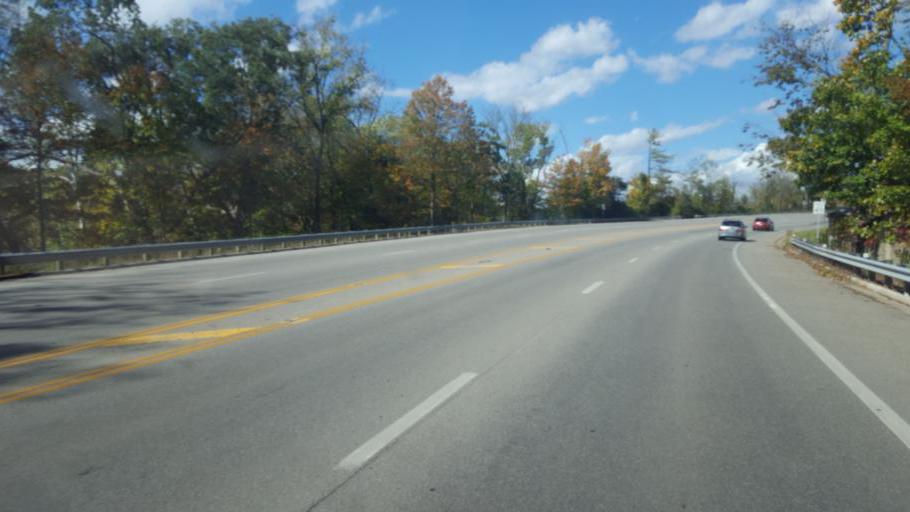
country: US
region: Ohio
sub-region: Delaware County
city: Powell
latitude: 40.1512
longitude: -83.1236
